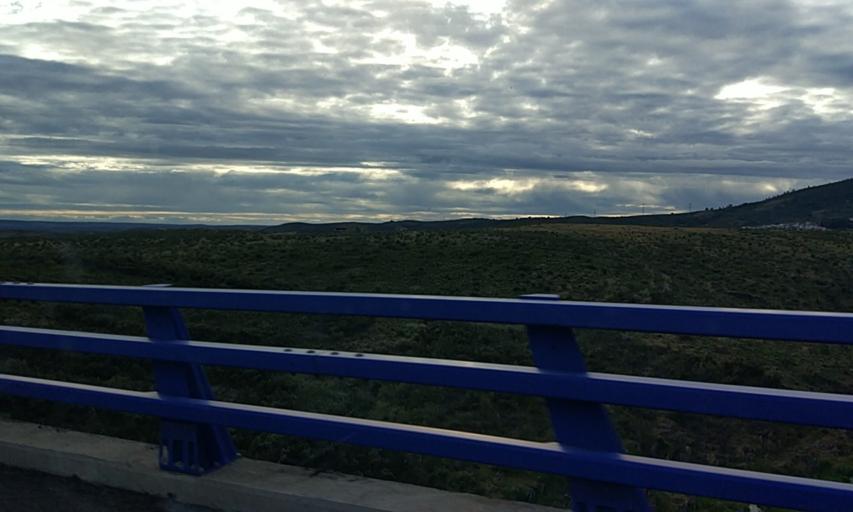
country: ES
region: Extremadura
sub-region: Provincia de Caceres
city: Canaveral
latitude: 39.7861
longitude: -6.3700
